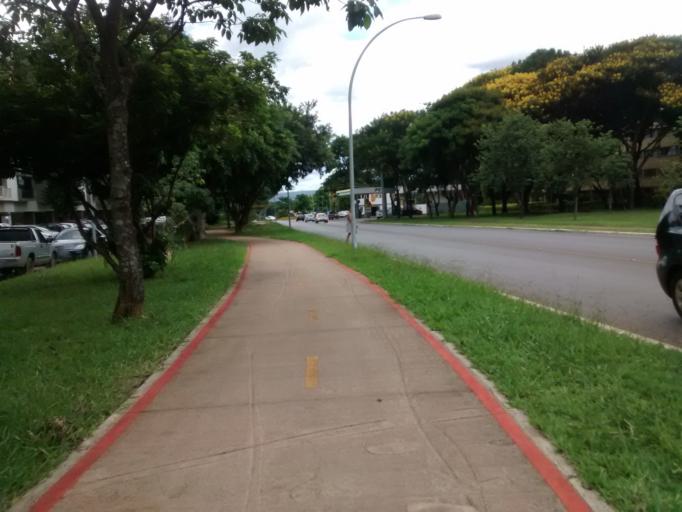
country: BR
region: Federal District
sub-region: Brasilia
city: Brasilia
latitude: -15.7560
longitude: -47.8825
